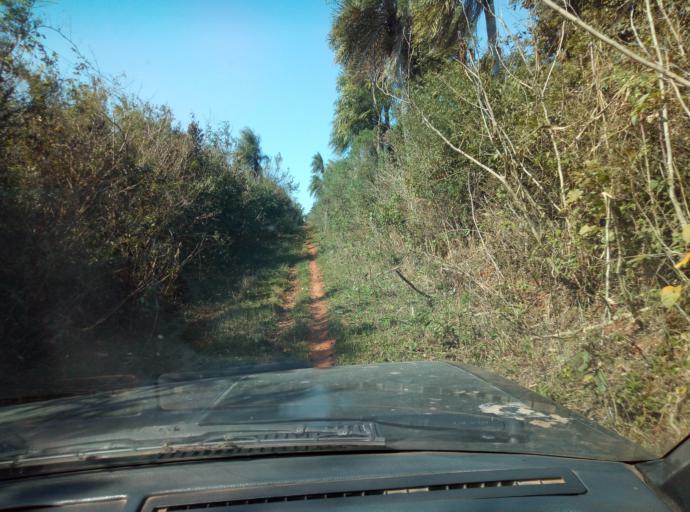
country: PY
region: Caaguazu
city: Doctor Cecilio Baez
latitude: -25.1793
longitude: -56.2190
